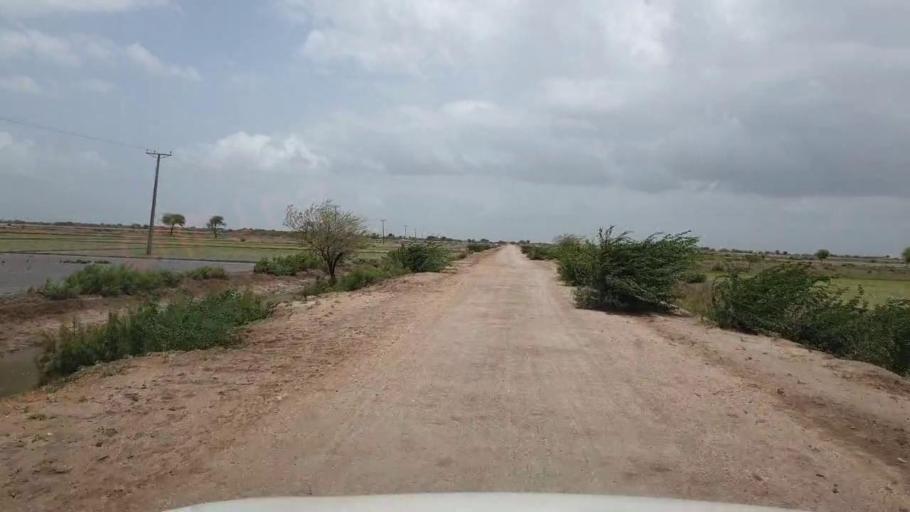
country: PK
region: Sindh
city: Kario
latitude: 24.6987
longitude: 68.6353
